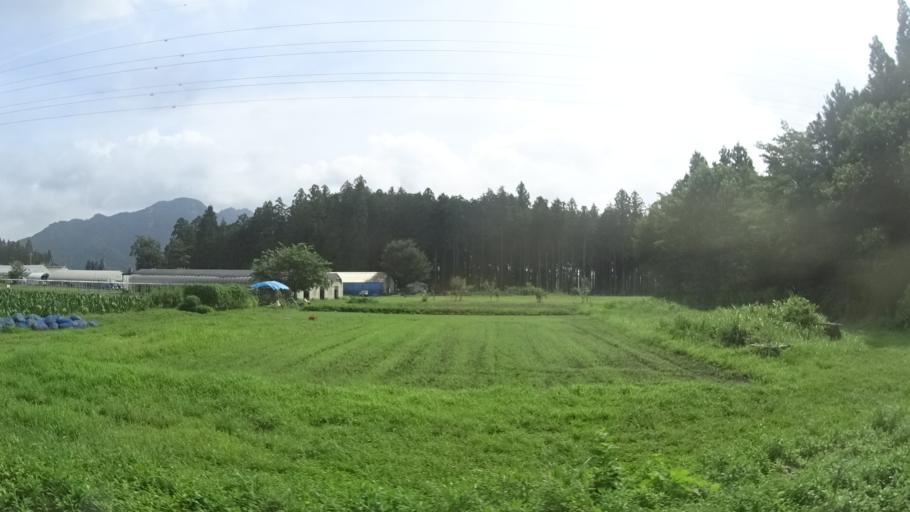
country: JP
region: Tochigi
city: Kanuma
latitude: 36.6030
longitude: 139.7454
